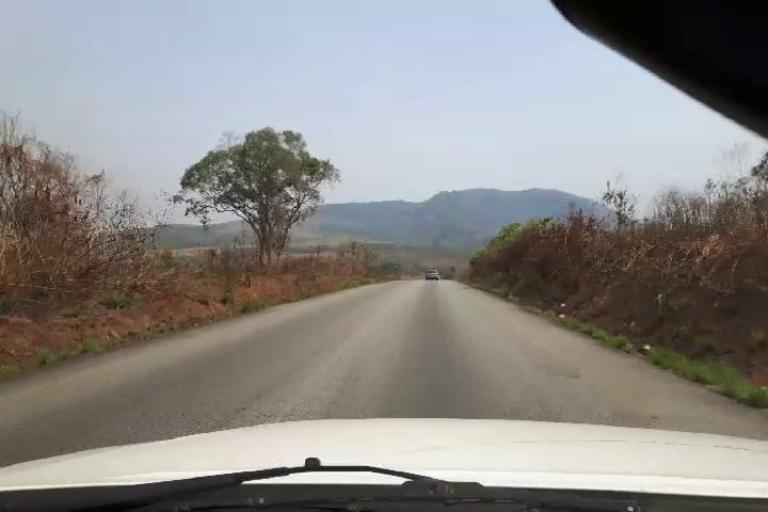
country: SL
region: Northern Province
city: Yonibana
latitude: 8.3888
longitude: -12.1912
